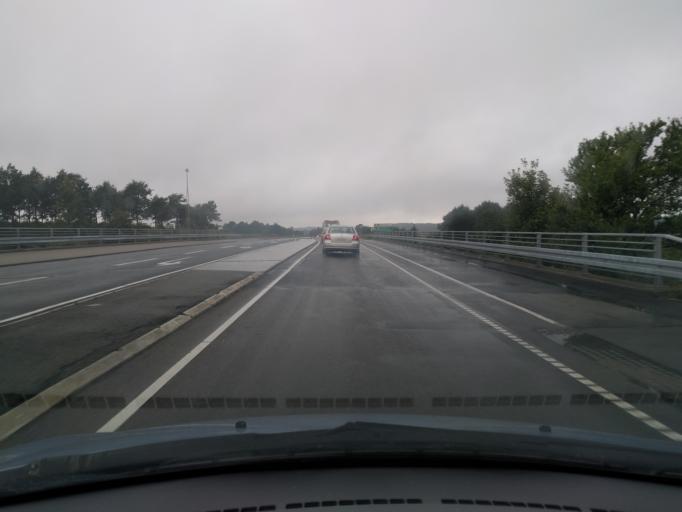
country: DK
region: Zealand
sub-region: Vordingborg Kommune
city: Nyrad
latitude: 55.0000
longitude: 11.9938
